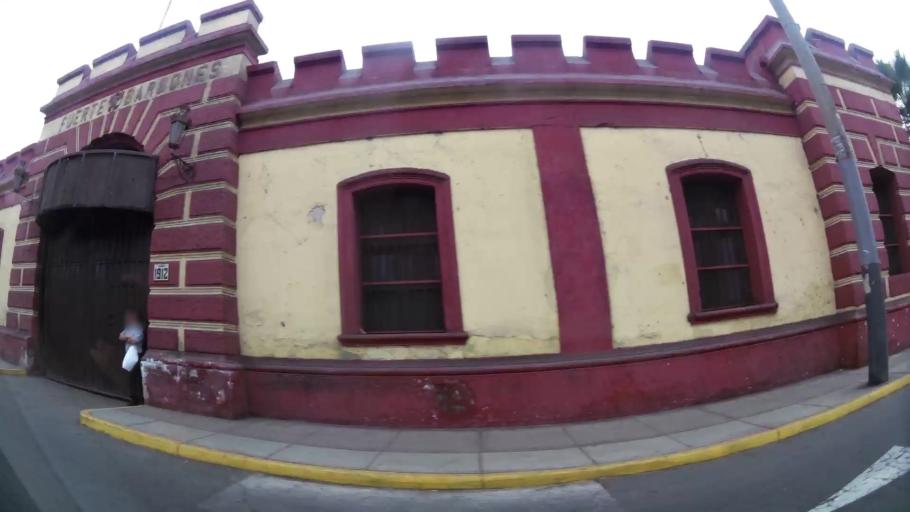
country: PE
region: Lima
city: Lima
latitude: -12.0526
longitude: -77.0114
